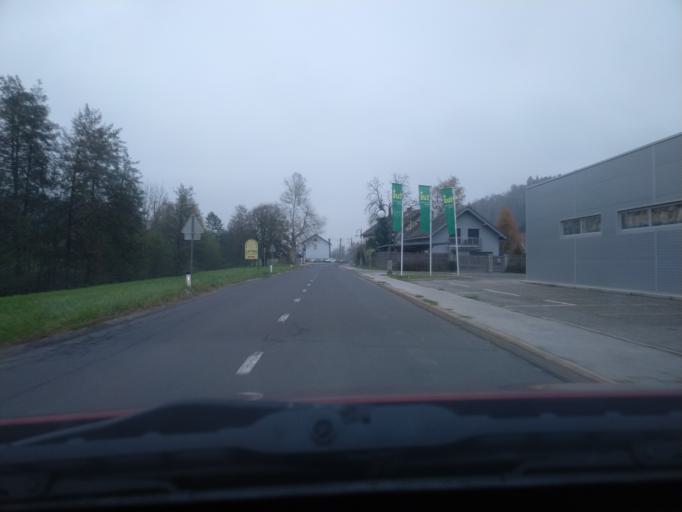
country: SI
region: Kungota
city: Zgornja Kungota
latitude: 46.6397
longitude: 15.6137
